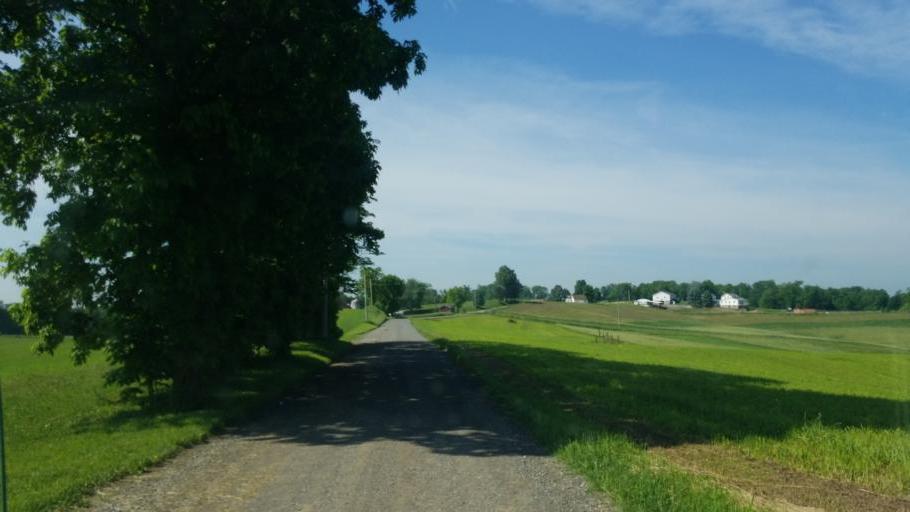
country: US
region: Ohio
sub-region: Tuscarawas County
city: Sugarcreek
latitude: 40.4579
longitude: -81.7638
